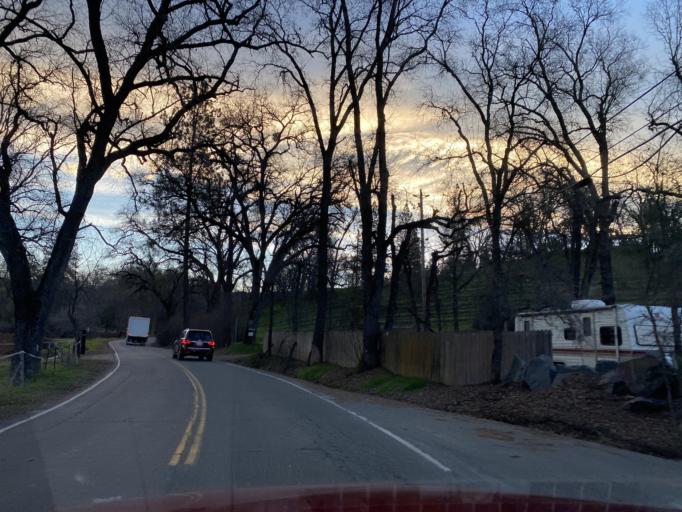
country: US
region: California
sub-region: Amador County
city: Plymouth
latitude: 38.5051
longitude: -120.7664
